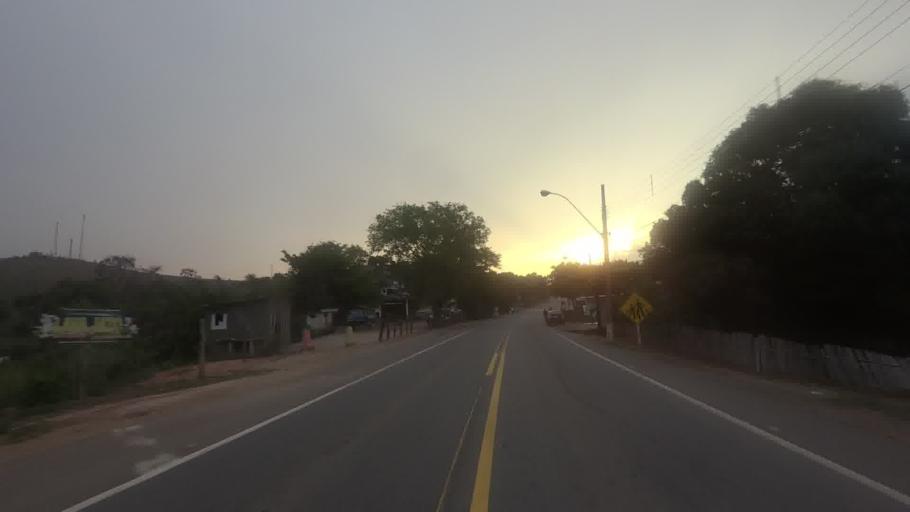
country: BR
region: Minas Gerais
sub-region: Recreio
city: Recreio
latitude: -21.7461
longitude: -42.4612
